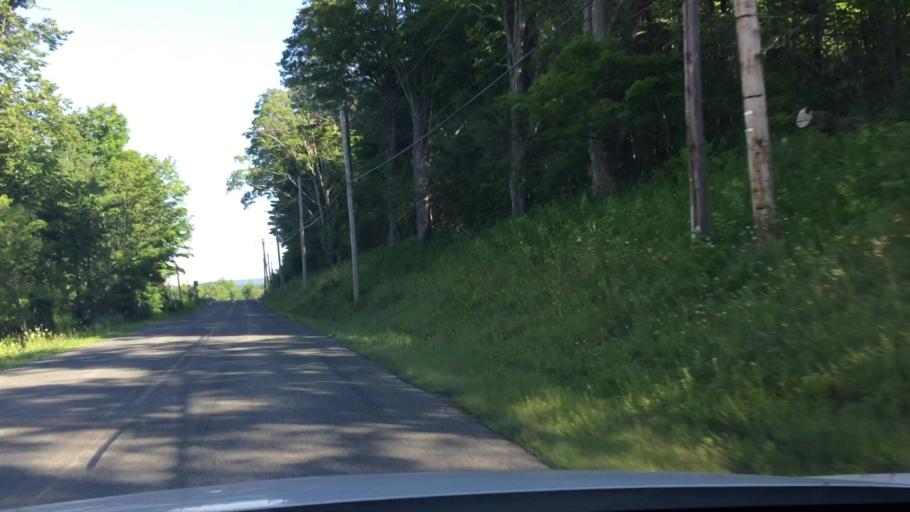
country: US
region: Massachusetts
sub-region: Berkshire County
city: Lee
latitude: 42.2682
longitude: -73.2331
